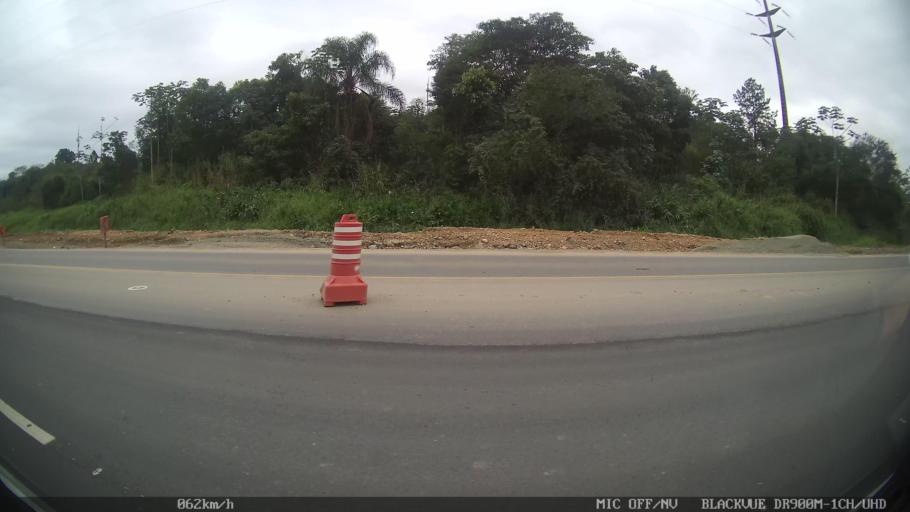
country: BR
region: Santa Catarina
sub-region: Joinville
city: Joinville
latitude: -26.2566
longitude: -48.8801
